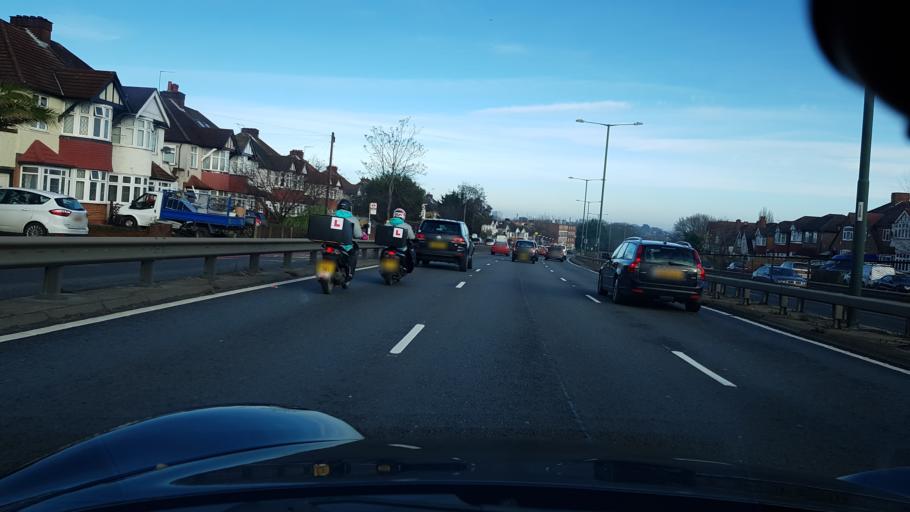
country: GB
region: England
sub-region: Greater London
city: New Malden
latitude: 51.3858
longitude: -0.2740
